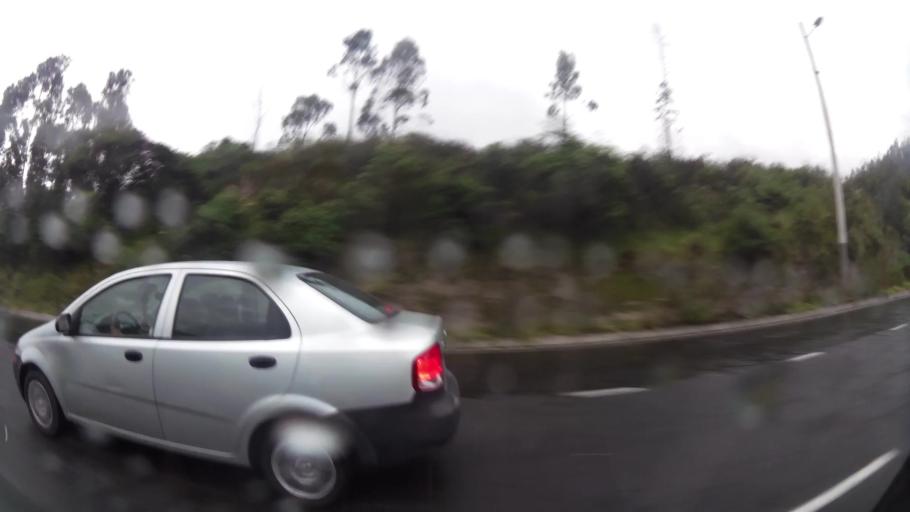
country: EC
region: Pichincha
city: Quito
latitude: -0.1397
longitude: -78.4459
